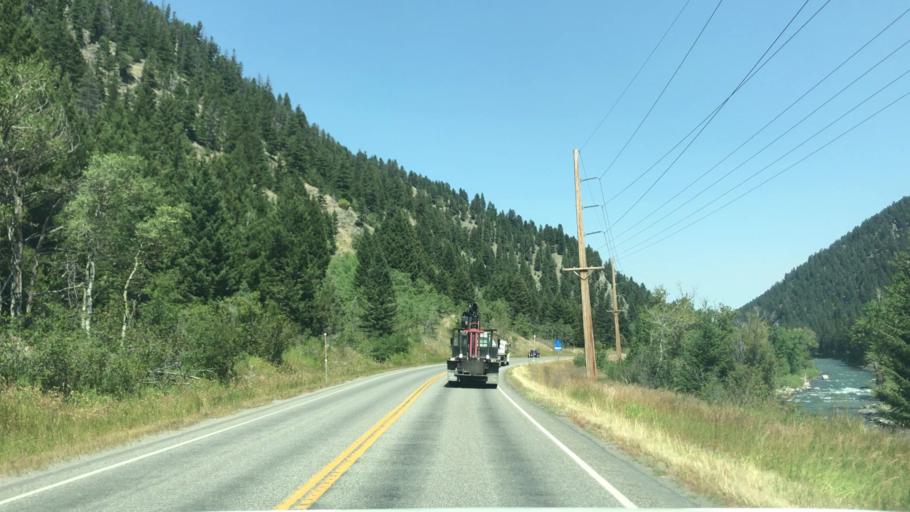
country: US
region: Montana
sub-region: Gallatin County
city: Four Corners
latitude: 45.5039
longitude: -111.2673
